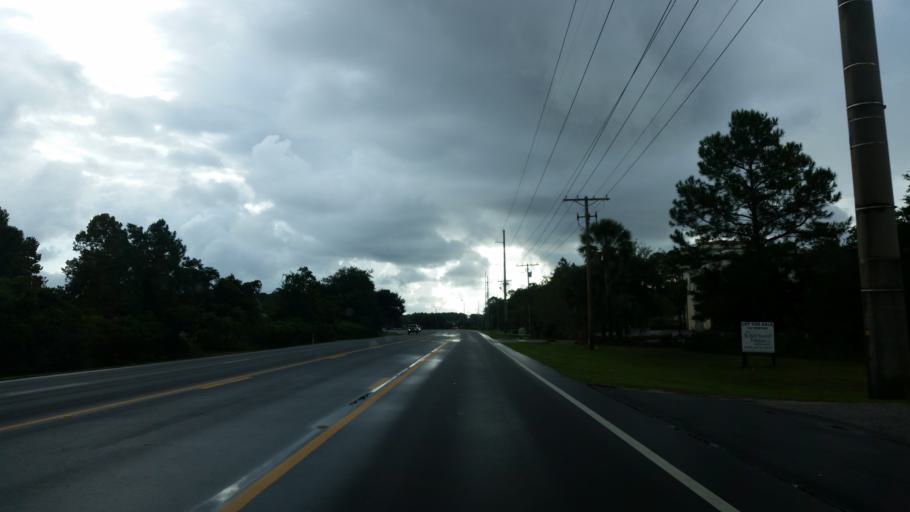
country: US
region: Alabama
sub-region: Baldwin County
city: Orange Beach
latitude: 30.2903
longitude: -87.5899
